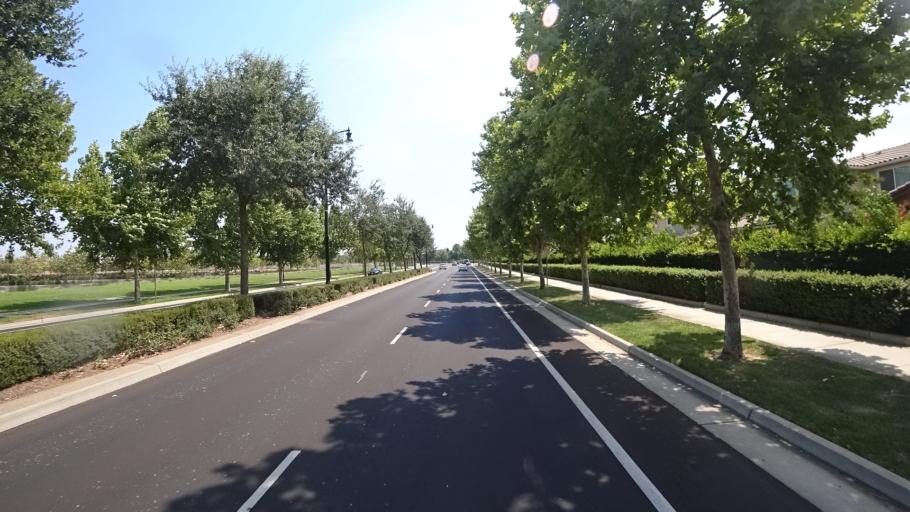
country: US
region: California
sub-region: Sacramento County
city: Laguna
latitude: 38.4048
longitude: -121.4045
